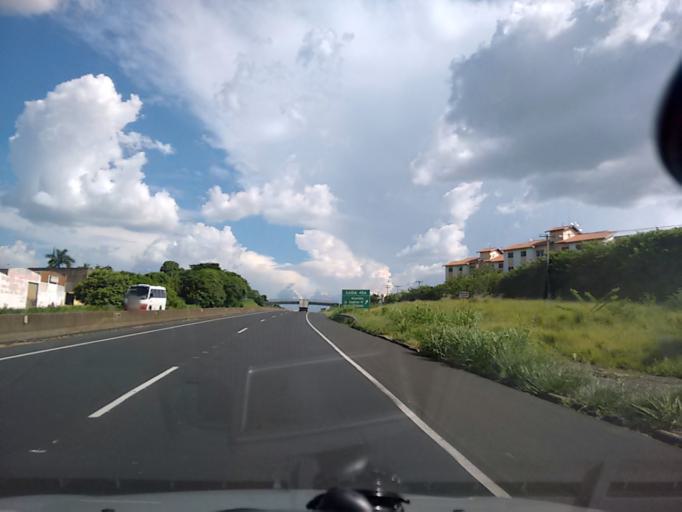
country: BR
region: Sao Paulo
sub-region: Marilia
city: Marilia
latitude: -22.1924
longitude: -49.9664
